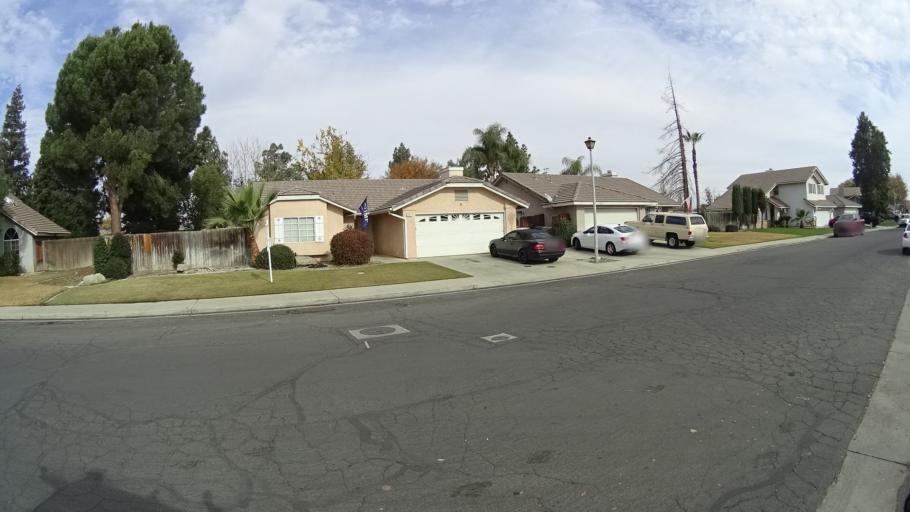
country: US
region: California
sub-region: Kern County
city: Rosedale
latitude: 35.3902
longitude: -119.1300
